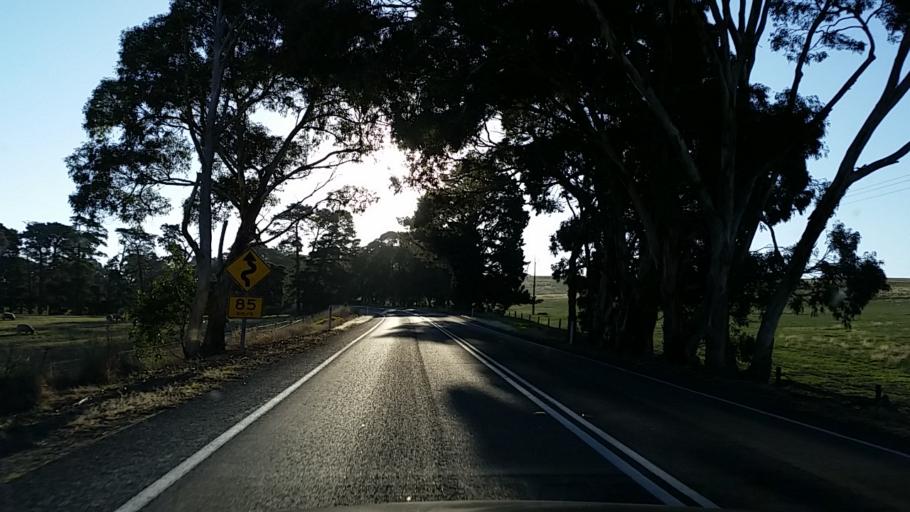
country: AU
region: South Australia
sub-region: Alexandrina
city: Goolwa
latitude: -35.3912
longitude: 138.7594
